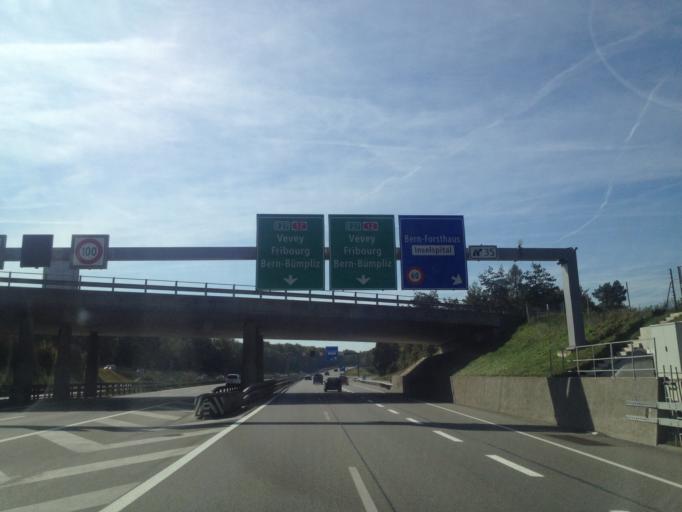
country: CH
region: Bern
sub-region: Bern-Mittelland District
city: Koniz
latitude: 46.9550
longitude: 7.4163
